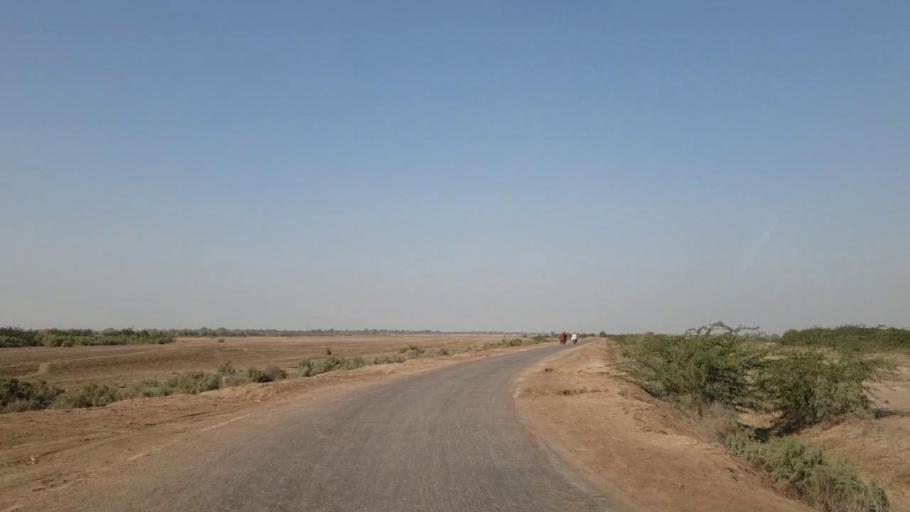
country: PK
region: Sindh
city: Digri
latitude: 24.9725
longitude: 69.1128
